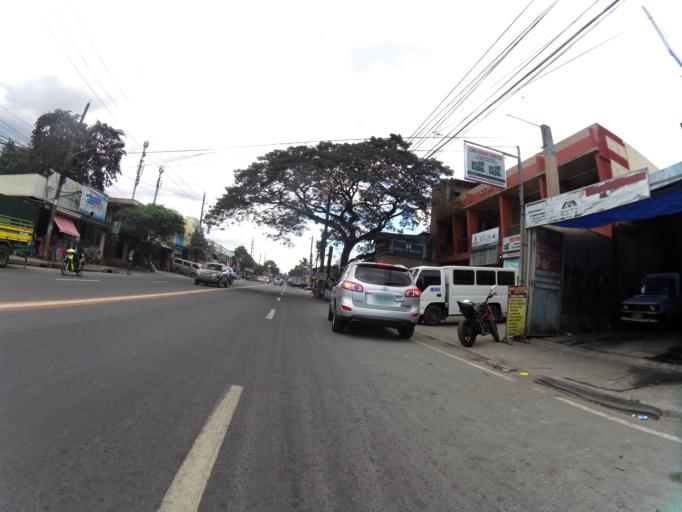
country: PH
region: Calabarzon
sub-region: Province of Rizal
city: Antipolo
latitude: 14.6323
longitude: 121.1153
